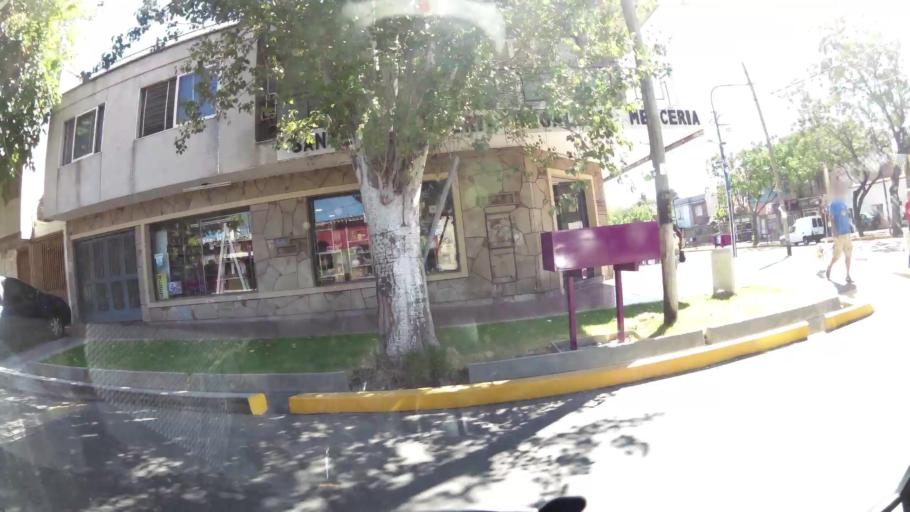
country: AR
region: Mendoza
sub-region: Departamento de Godoy Cruz
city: Godoy Cruz
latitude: -32.9045
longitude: -68.8605
